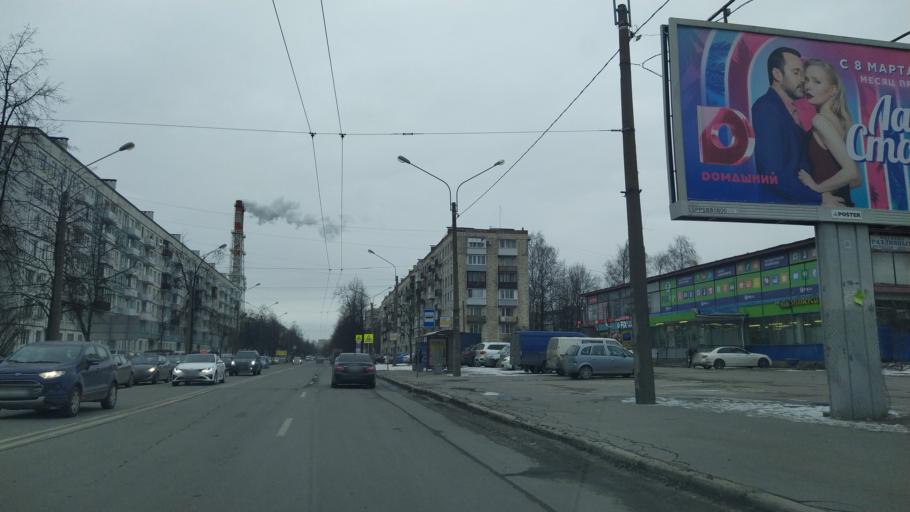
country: RU
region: Leningrad
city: Kalininskiy
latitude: 59.9536
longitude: 30.4221
